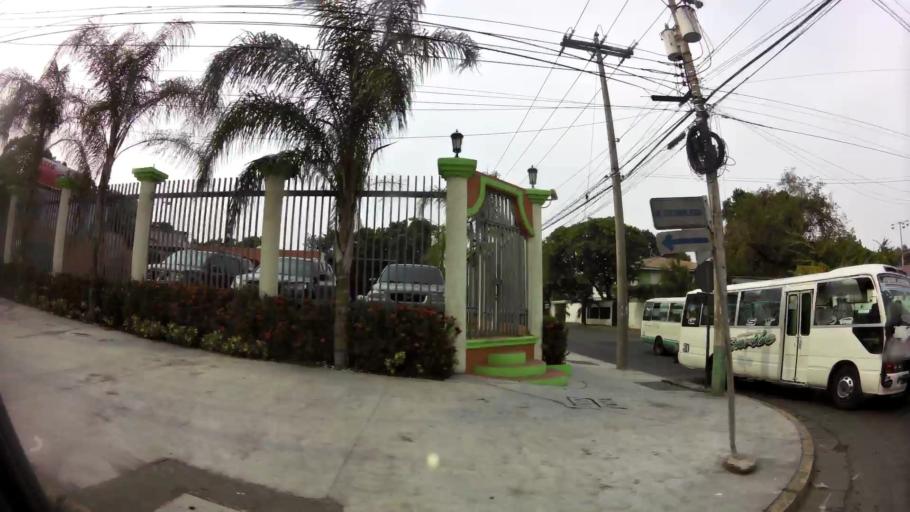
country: HN
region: Cortes
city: San Pedro Sula
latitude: 15.4911
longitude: -88.0298
